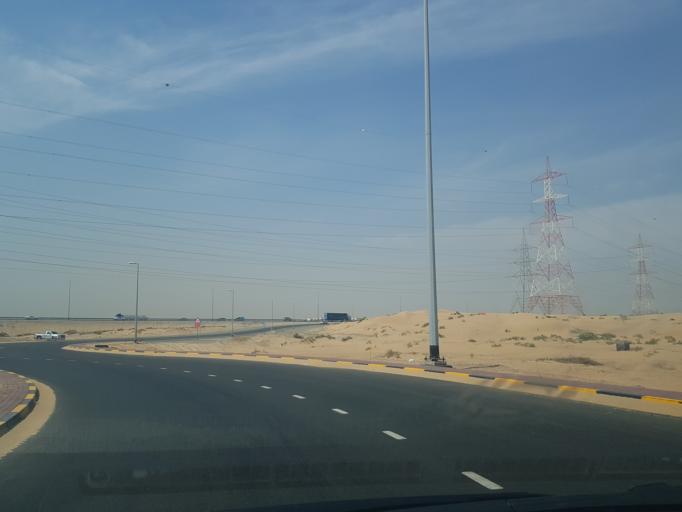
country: AE
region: Ash Shariqah
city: Sharjah
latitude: 25.2863
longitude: 55.5912
